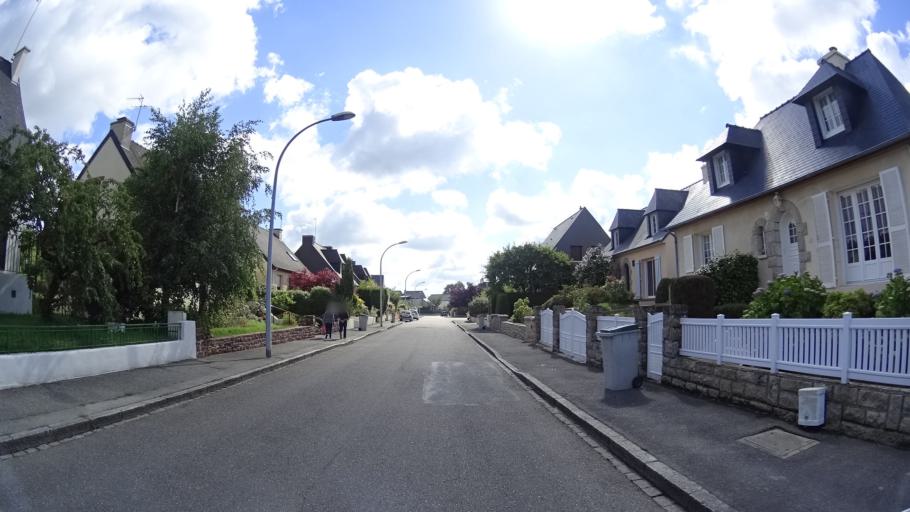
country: FR
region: Brittany
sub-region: Departement d'Ille-et-Vilaine
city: Saint-Gilles
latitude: 48.1290
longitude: -1.8146
